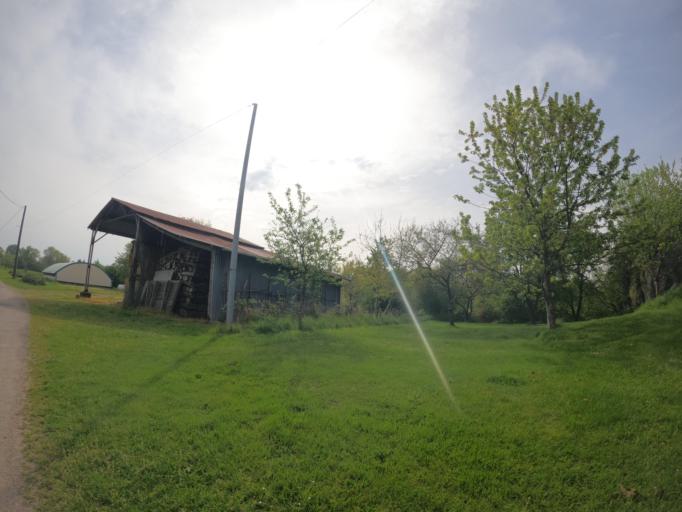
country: FR
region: Poitou-Charentes
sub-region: Departement des Deux-Sevres
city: Moncoutant
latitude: 46.6964
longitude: -0.5264
